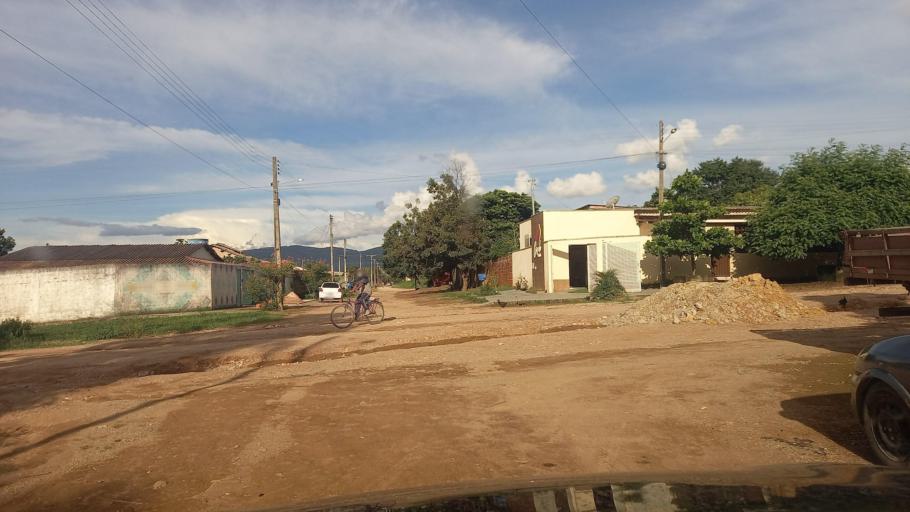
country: BR
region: Goias
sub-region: Cavalcante
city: Cavalcante
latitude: -13.7934
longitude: -47.4417
